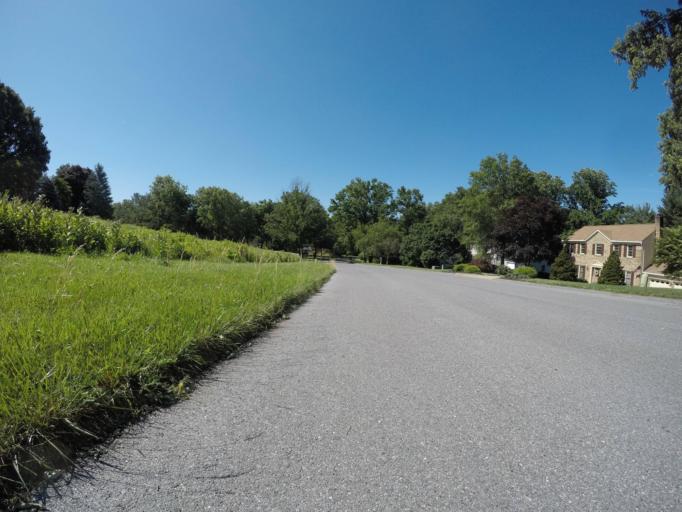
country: US
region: Maryland
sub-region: Howard County
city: Columbia
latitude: 39.2303
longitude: -76.8685
